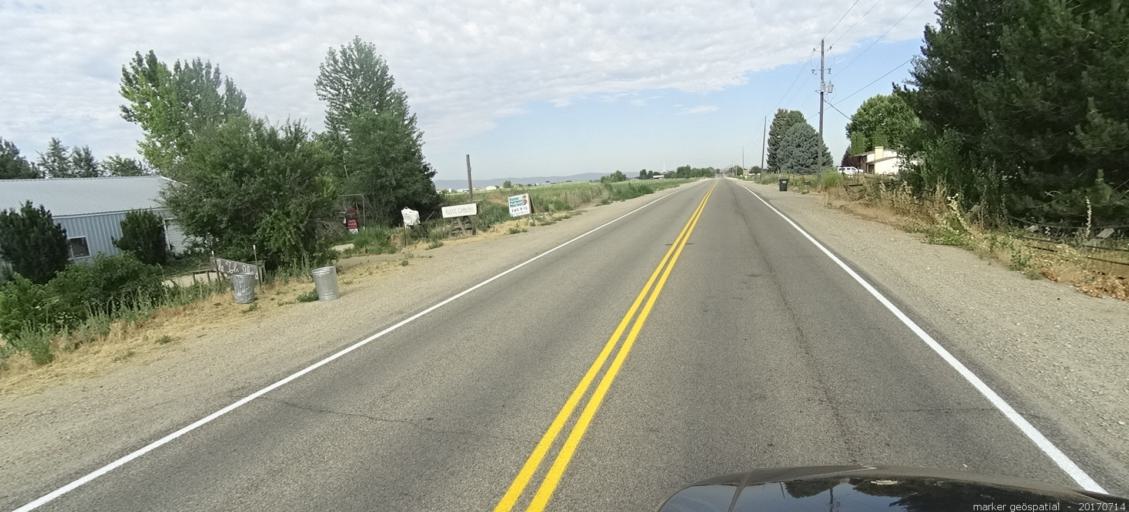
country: US
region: Idaho
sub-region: Ada County
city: Kuna
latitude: 43.4884
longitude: -116.4442
